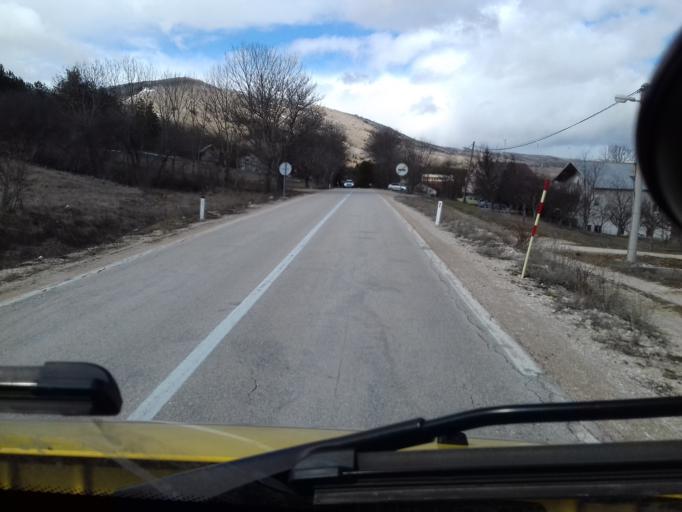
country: BA
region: Federation of Bosnia and Herzegovina
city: Dreznica
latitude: 43.5867
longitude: 17.2812
